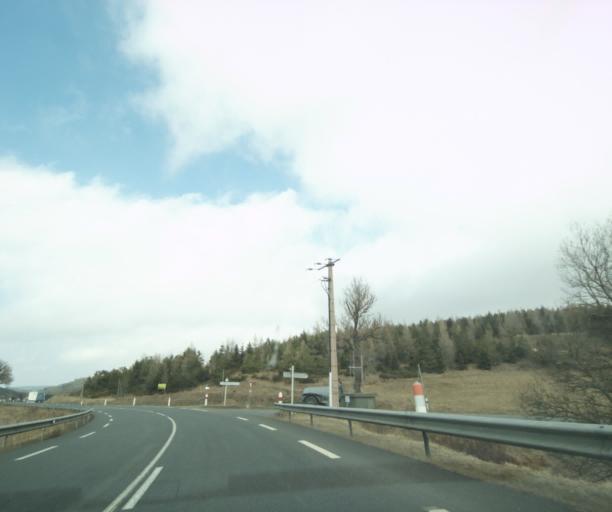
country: FR
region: Languedoc-Roussillon
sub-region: Departement de la Lozere
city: Langogne
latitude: 44.6266
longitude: 3.6755
